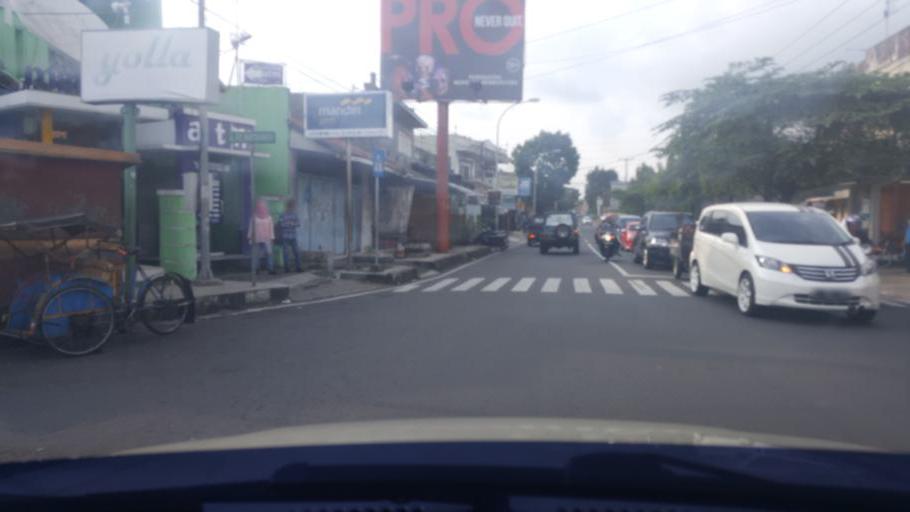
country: ID
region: West Java
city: Tawangsari
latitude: -7.3199
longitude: 108.2197
